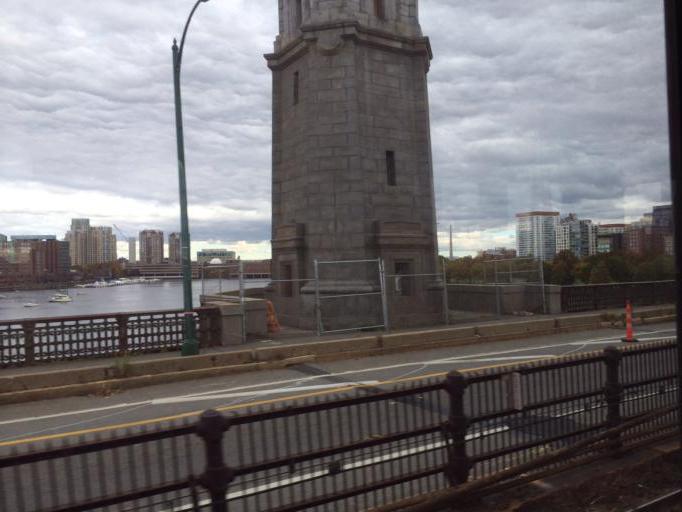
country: US
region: Massachusetts
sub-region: Suffolk County
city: Boston
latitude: 42.3616
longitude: -71.0760
